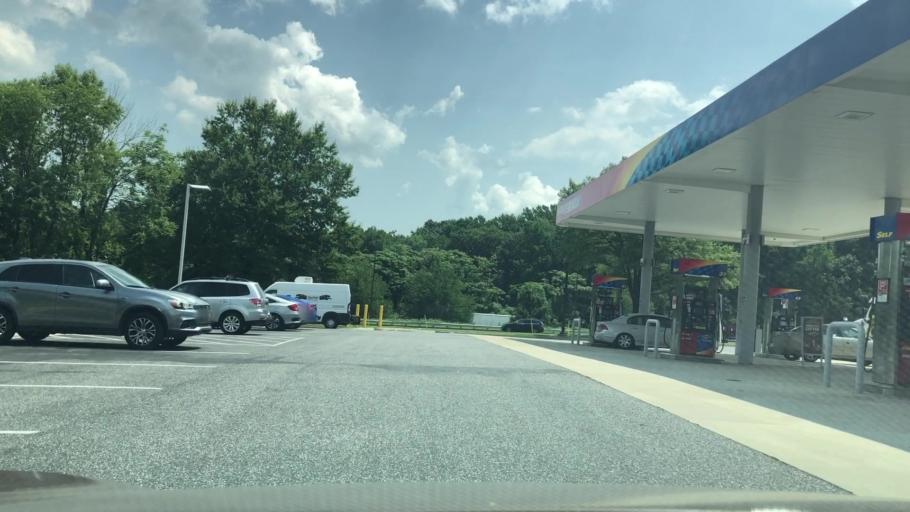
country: US
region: Maryland
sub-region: Harford County
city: Riverside
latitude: 39.4989
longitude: -76.2303
